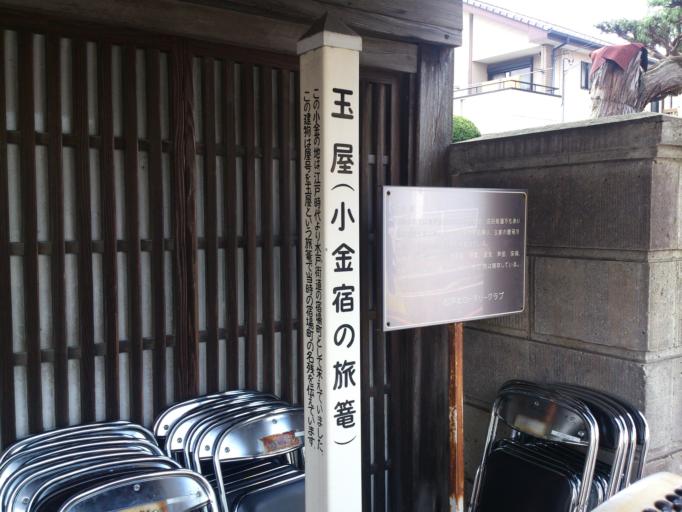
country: JP
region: Chiba
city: Nagareyama
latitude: 35.8264
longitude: 139.9325
